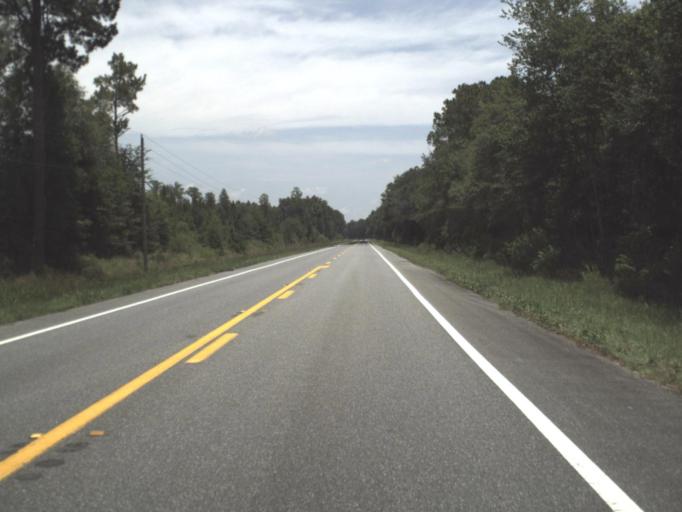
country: US
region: Florida
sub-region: Lafayette County
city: Mayo
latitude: 29.9811
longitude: -83.2012
